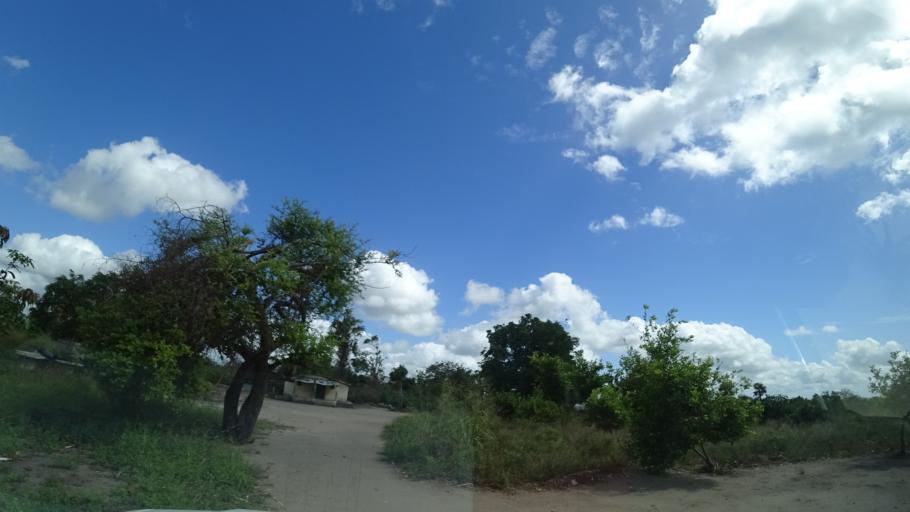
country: MZ
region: Sofala
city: Dondo
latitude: -19.3594
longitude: 34.5720
